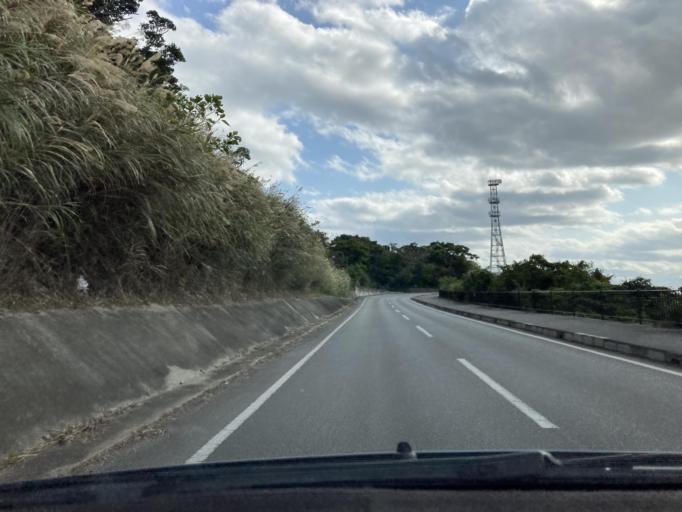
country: JP
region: Okinawa
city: Tomigusuku
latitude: 26.1730
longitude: 127.7602
